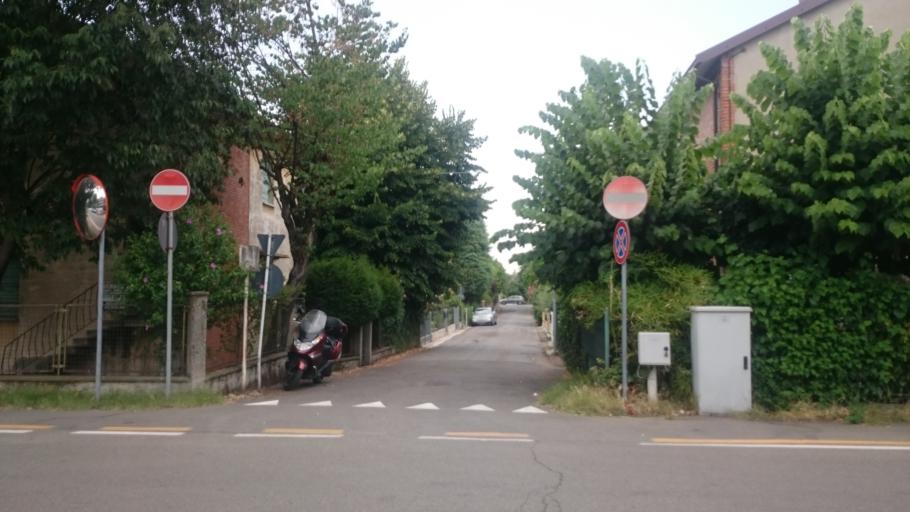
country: IT
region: Emilia-Romagna
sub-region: Provincia di Reggio Emilia
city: Scandiano
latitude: 44.5999
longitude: 10.6920
